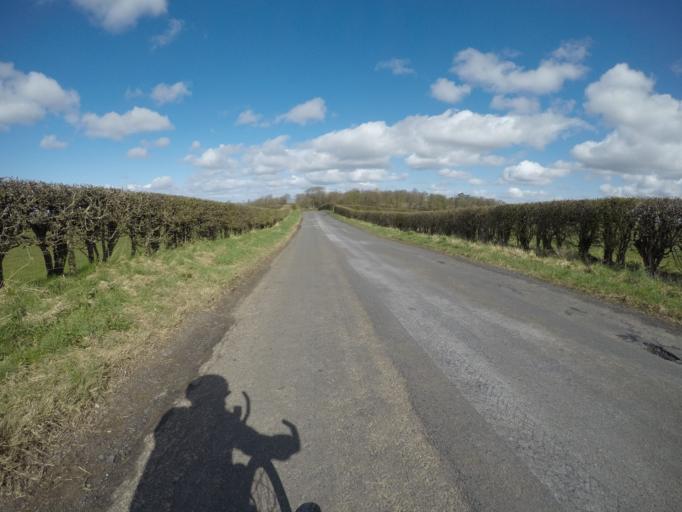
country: GB
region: Scotland
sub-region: East Ayrshire
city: Crosshouse
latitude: 55.6086
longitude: -4.5759
